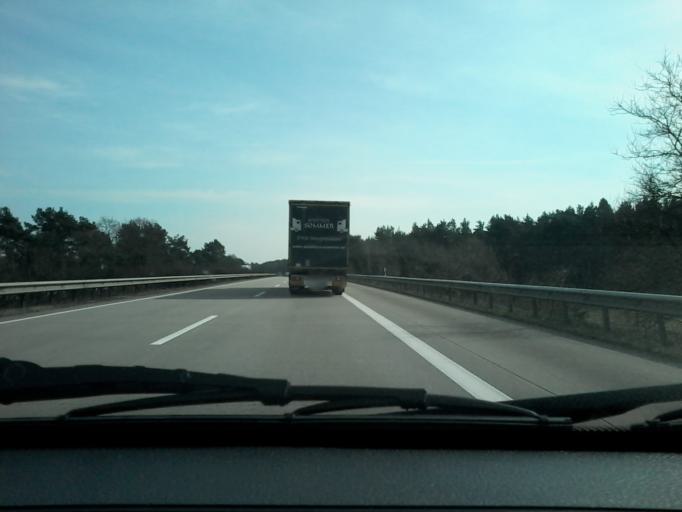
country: DE
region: Lower Saxony
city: Verden
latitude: 52.9443
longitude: 9.2611
